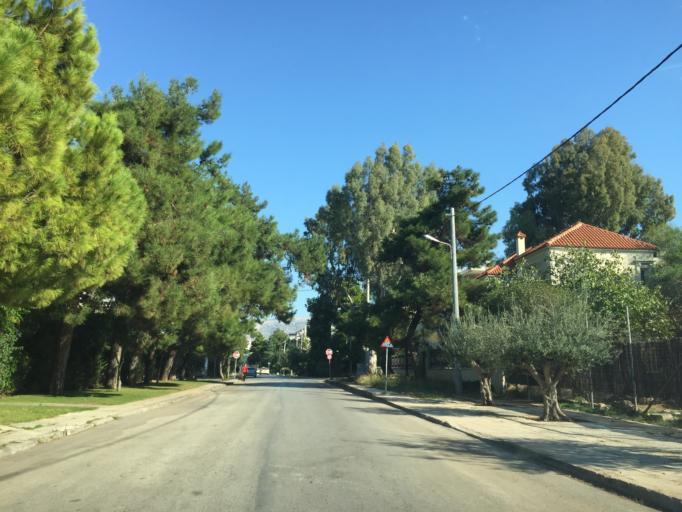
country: GR
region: Attica
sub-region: Nomarchia Athinas
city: Glyfada
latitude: 37.8557
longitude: 23.7556
